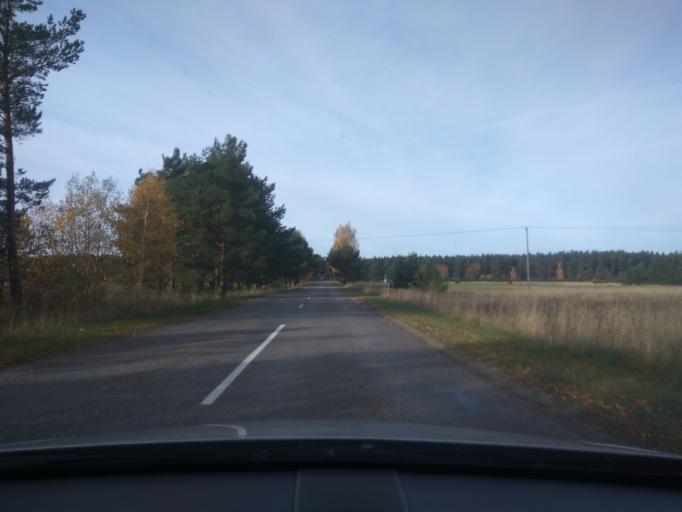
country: LV
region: Alsunga
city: Alsunga
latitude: 57.0111
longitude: 21.3975
